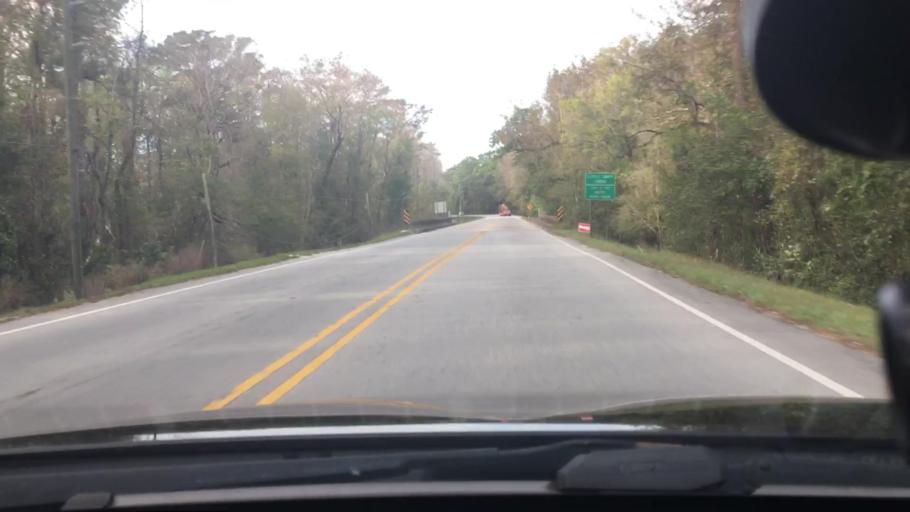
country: US
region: North Carolina
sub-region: Craven County
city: Vanceboro
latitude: 35.2315
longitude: -77.0725
